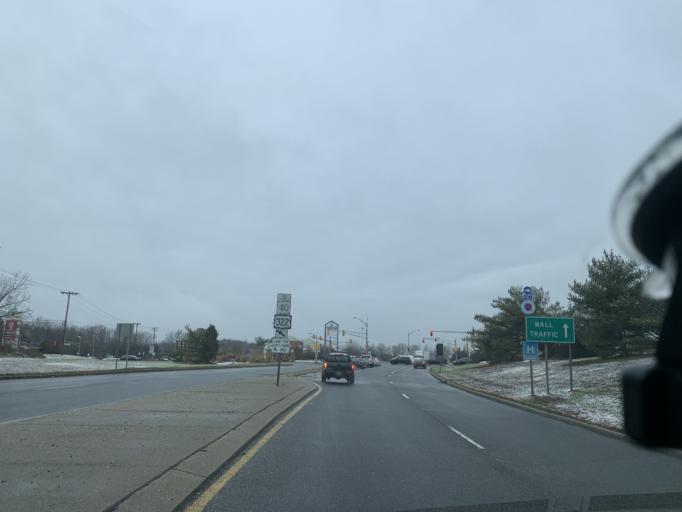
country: US
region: New Jersey
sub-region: Atlantic County
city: Pomona
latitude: 39.4498
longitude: -74.6364
